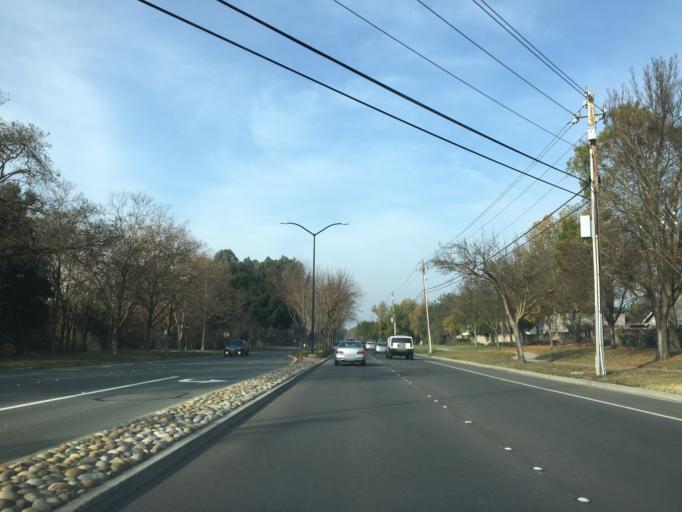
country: US
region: California
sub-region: Contra Costa County
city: Blackhawk
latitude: 37.8013
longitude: -121.9335
